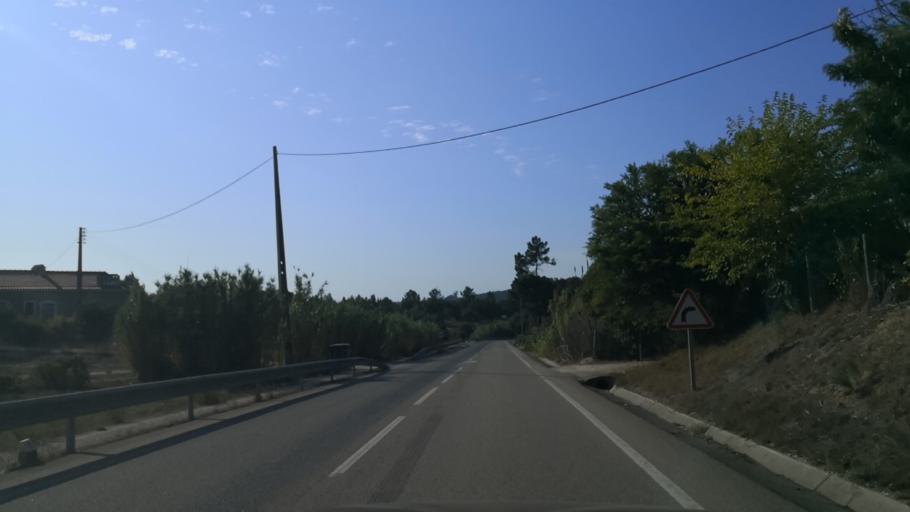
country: PT
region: Santarem
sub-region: Almeirim
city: Fazendas de Almeirim
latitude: 39.1046
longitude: -8.5785
